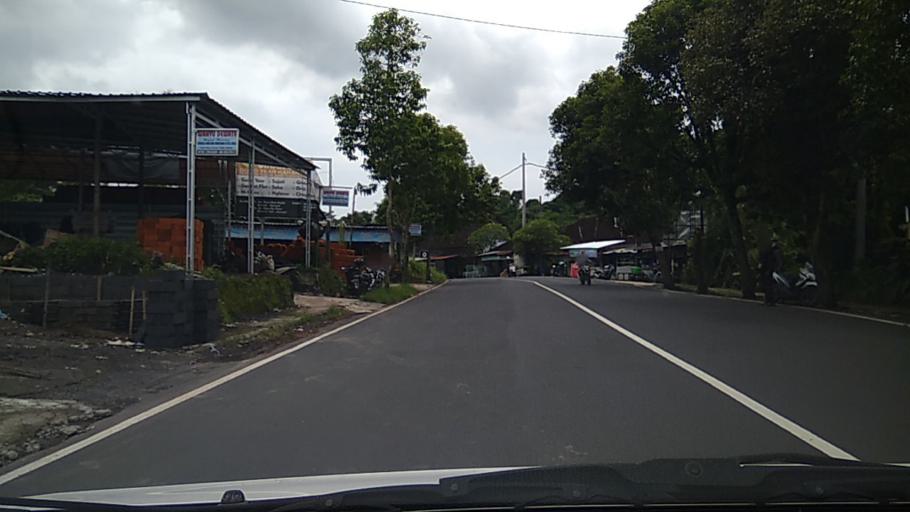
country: ID
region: Bali
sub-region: Kabupaten Gianyar
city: Ubud
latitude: -8.5229
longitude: 115.2885
